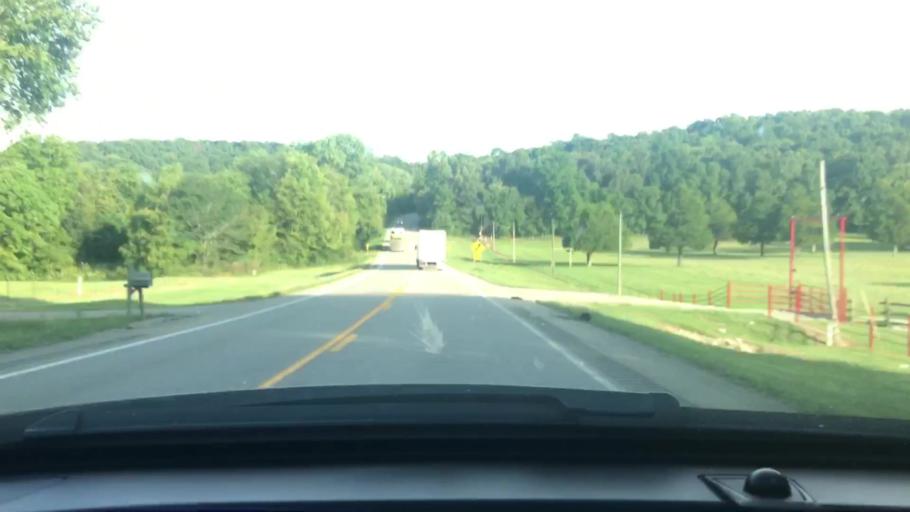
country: US
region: Arkansas
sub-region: Randolph County
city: Pocahontas
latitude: 36.2183
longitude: -91.2196
